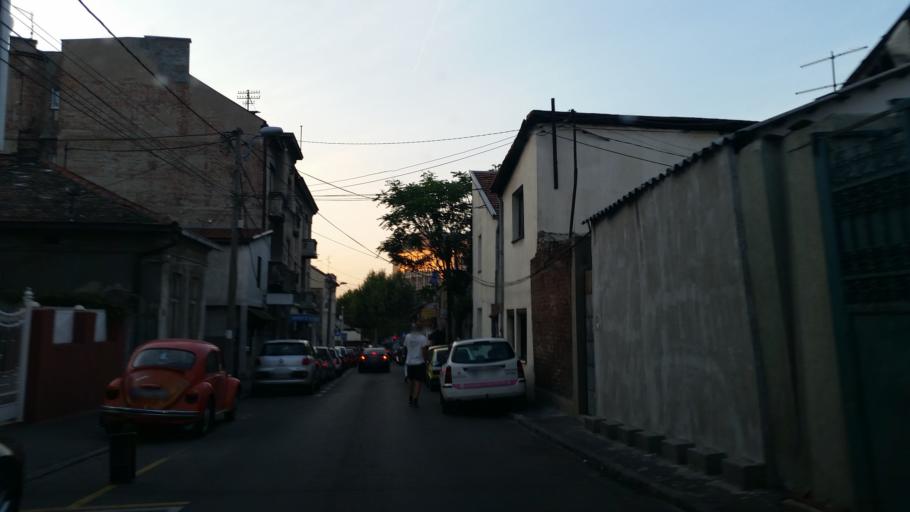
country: RS
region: Central Serbia
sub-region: Belgrade
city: Vracar
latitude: 44.8018
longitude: 20.4825
